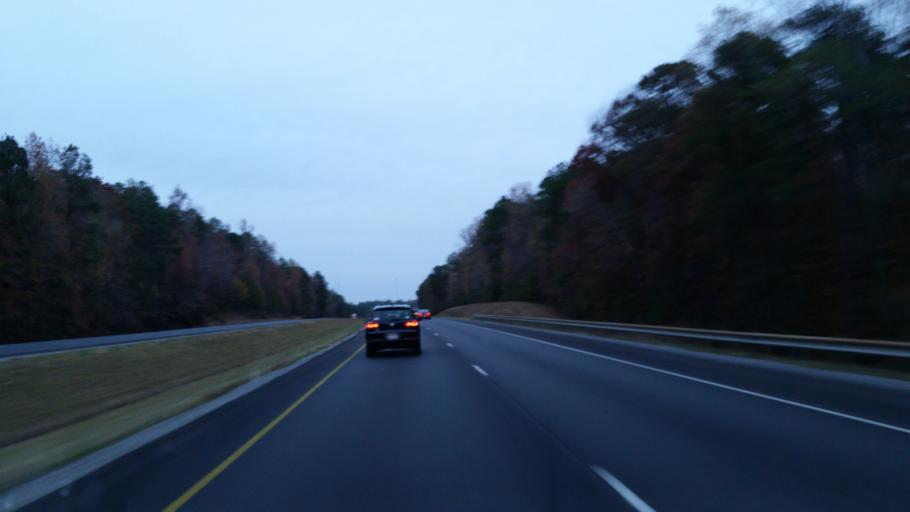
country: US
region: Alabama
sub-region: Greene County
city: Eutaw
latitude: 32.9707
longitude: -87.8072
